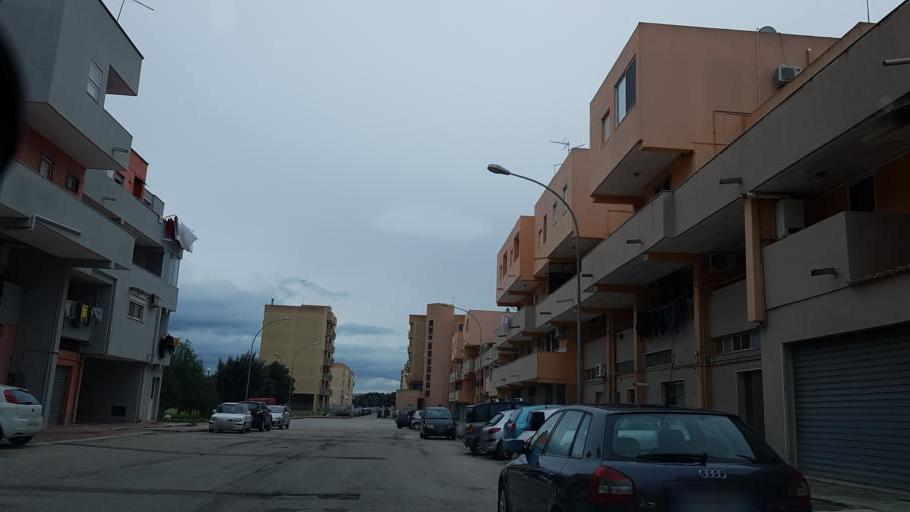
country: IT
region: Apulia
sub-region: Provincia di Brindisi
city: Brindisi
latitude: 40.6306
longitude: 17.9538
